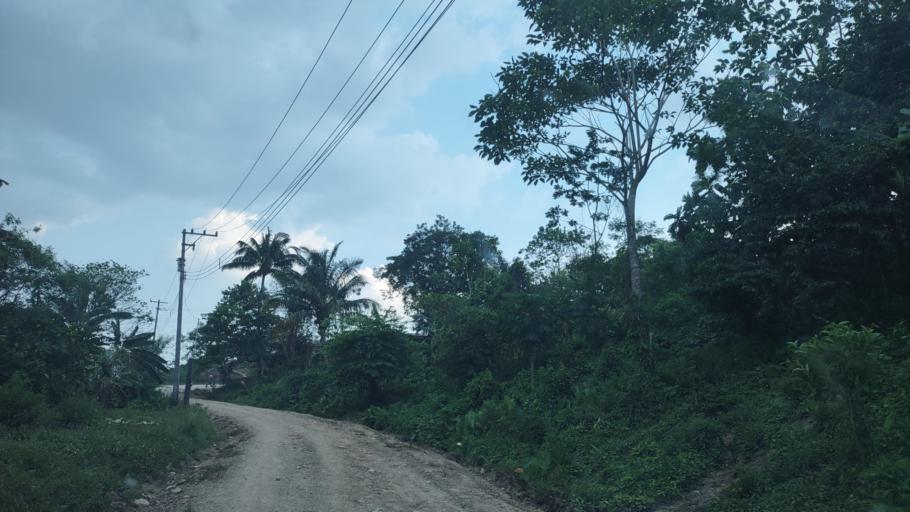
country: MX
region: Chiapas
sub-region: Tecpatan
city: Raudales Malpaso
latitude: 17.3097
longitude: -93.7783
